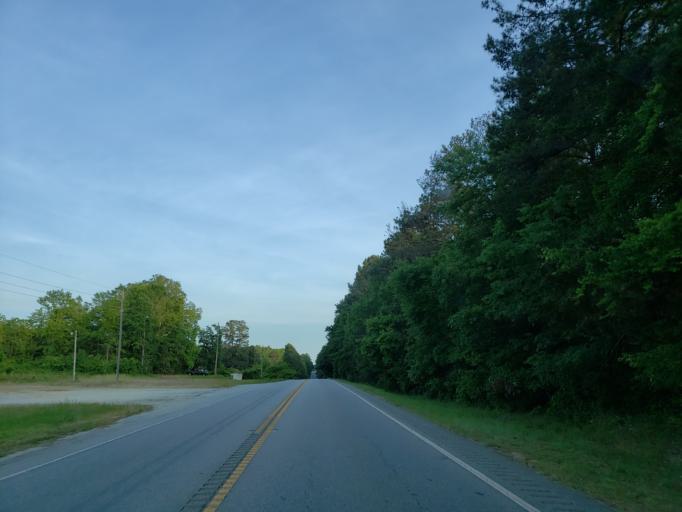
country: US
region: Georgia
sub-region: Coweta County
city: Newnan
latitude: 33.4554
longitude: -84.8867
